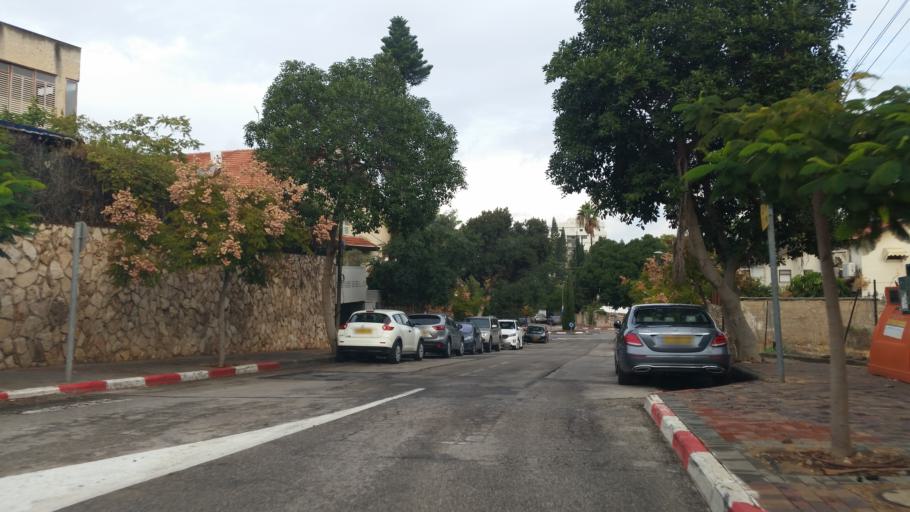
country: IL
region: Tel Aviv
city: Ramat HaSharon
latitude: 32.1568
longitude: 34.8475
